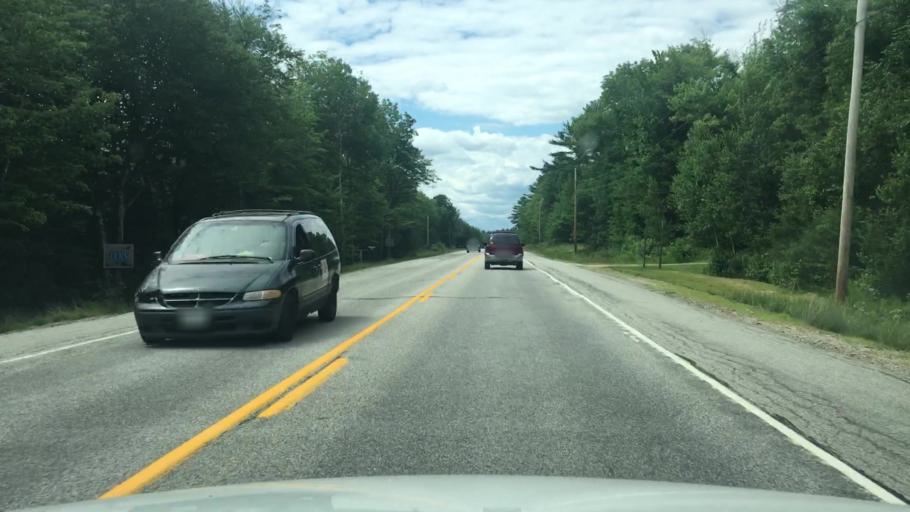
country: US
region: Maine
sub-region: Oxford County
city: West Paris
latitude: 44.3627
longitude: -70.5856
